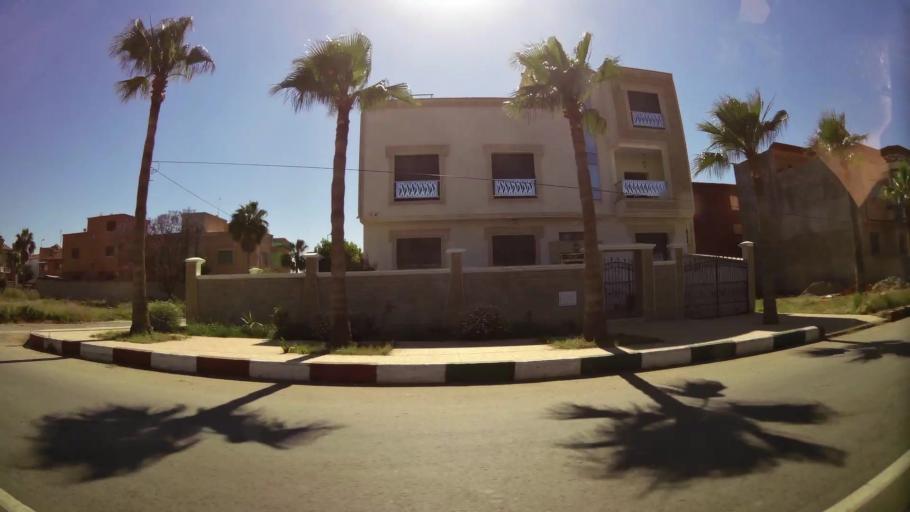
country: MA
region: Oriental
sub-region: Berkane-Taourirt
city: Berkane
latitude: 34.9417
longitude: -2.3254
